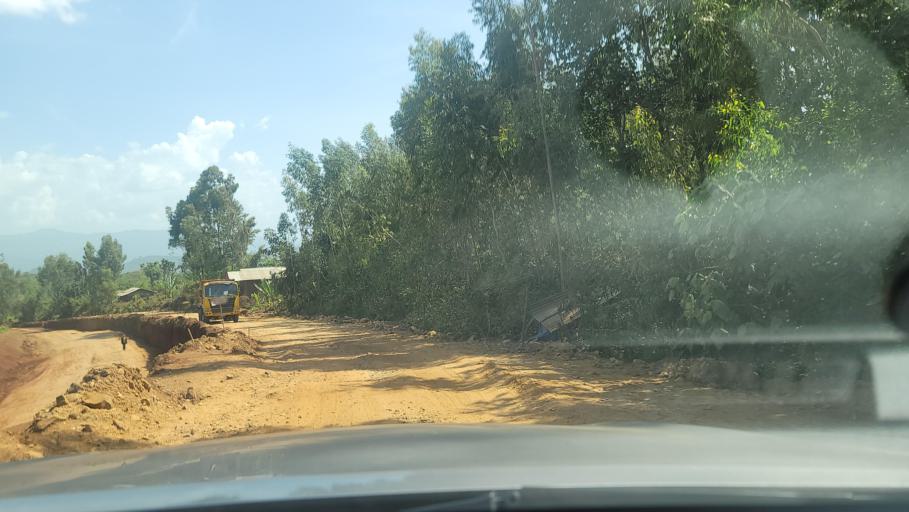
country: ET
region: Oromiya
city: Agaro
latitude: 7.8041
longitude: 36.4575
